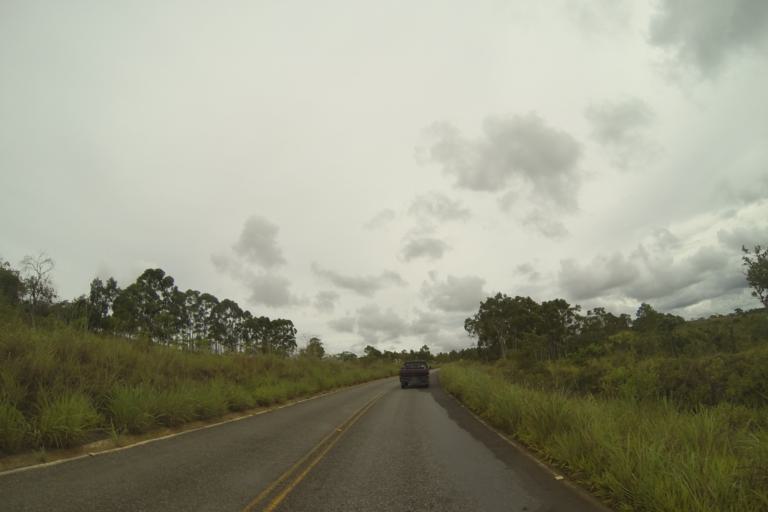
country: BR
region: Minas Gerais
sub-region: Ibia
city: Ibia
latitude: -19.6695
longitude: -46.4383
